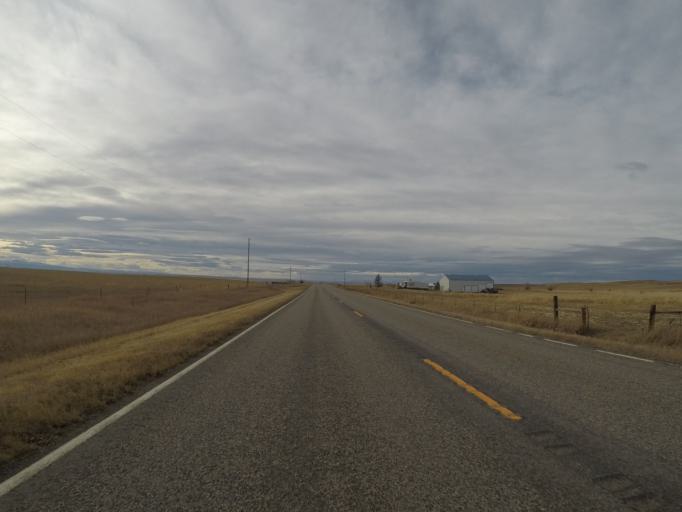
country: US
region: Montana
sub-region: Yellowstone County
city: Laurel
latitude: 45.8565
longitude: -108.8263
